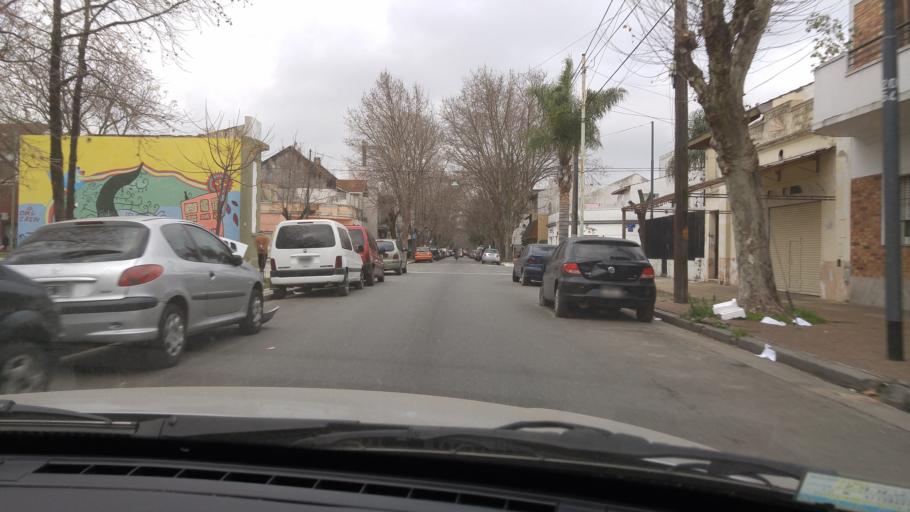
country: AR
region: Buenos Aires
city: Caseros
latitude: -34.6168
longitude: -58.5246
